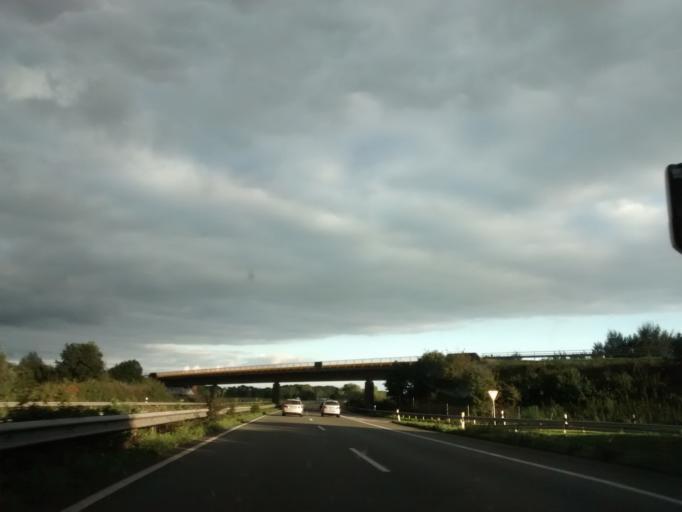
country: DE
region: Lower Saxony
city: Salzbergen
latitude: 52.3417
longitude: 7.3994
